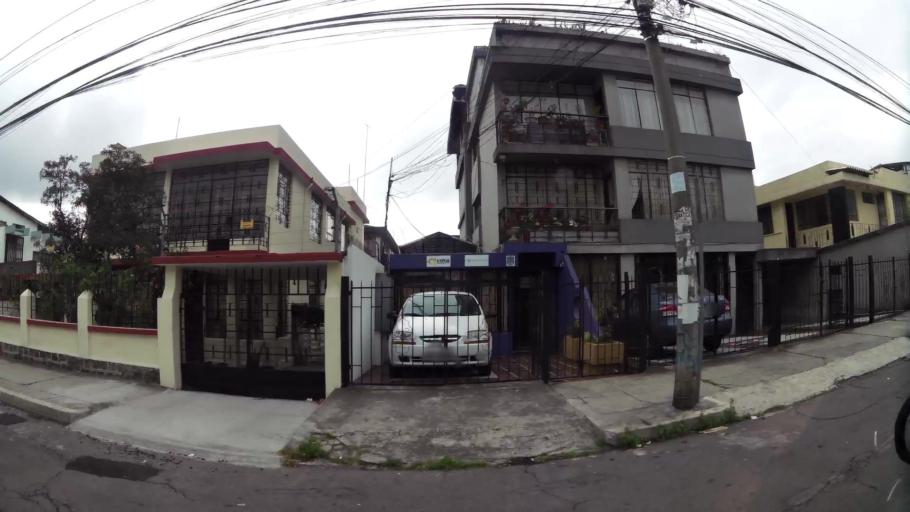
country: EC
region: Pichincha
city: Quito
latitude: -0.1887
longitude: -78.4902
